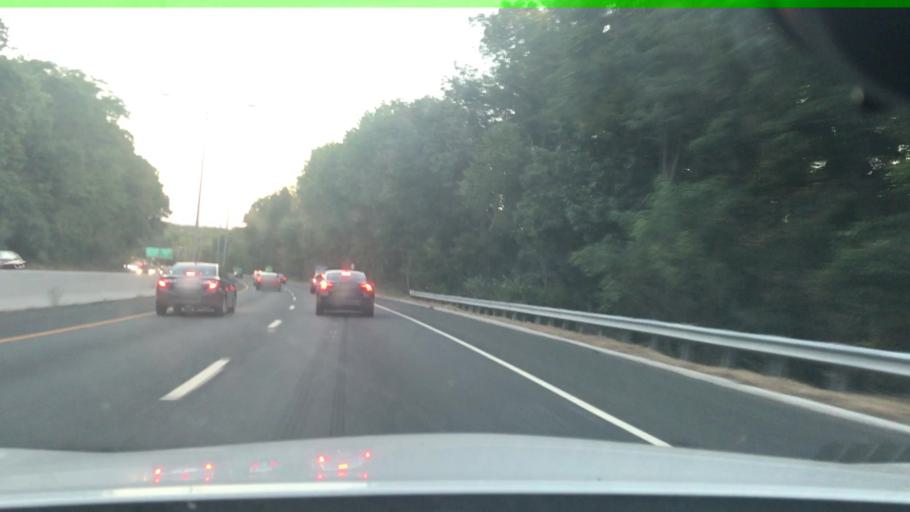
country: US
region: New Jersey
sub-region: Passaic County
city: Hawthorne
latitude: 40.9722
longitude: -74.1593
